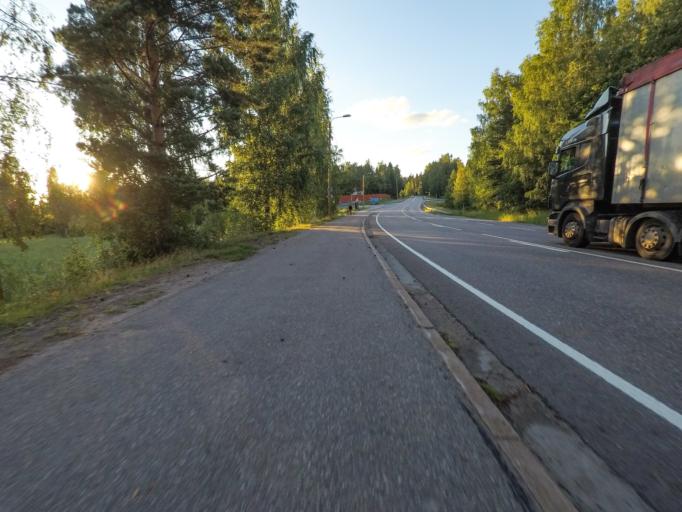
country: FI
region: South Karelia
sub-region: Imatra
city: Ruokolahti
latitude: 61.2879
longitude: 28.8412
